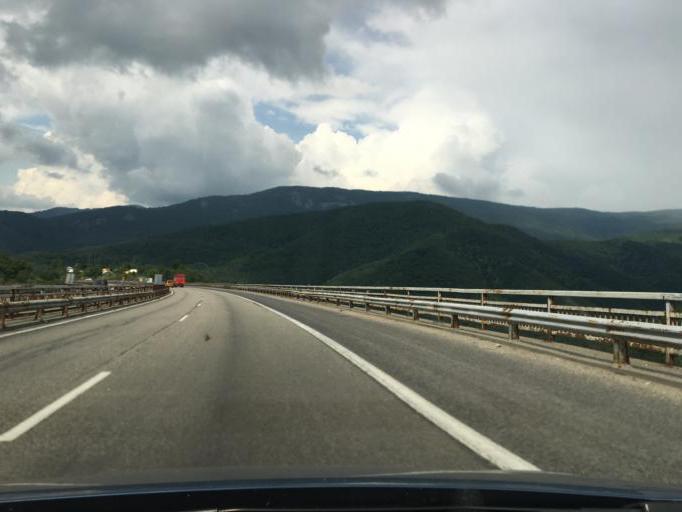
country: BG
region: Sofiya
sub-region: Obshtina Botevgrad
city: Botevgrad
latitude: 42.7959
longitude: 23.8098
